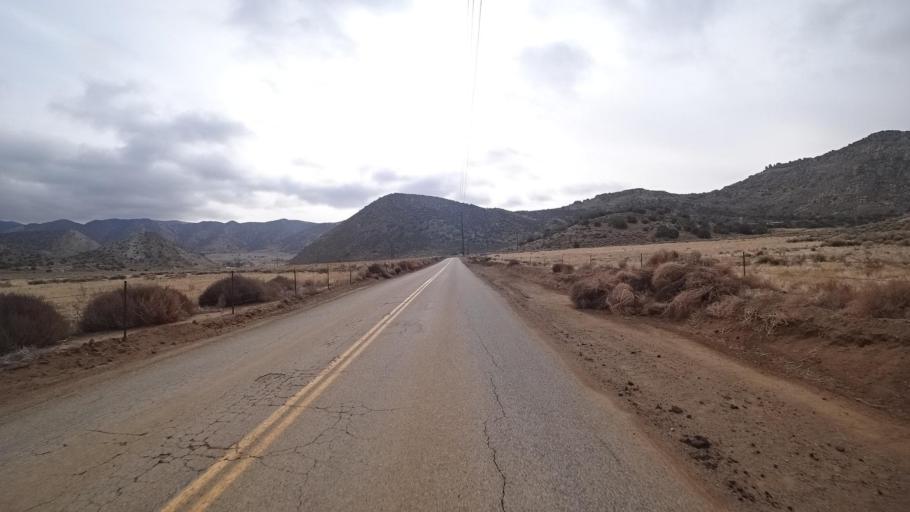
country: US
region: California
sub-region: Kern County
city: Tehachapi
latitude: 35.1549
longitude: -118.3203
